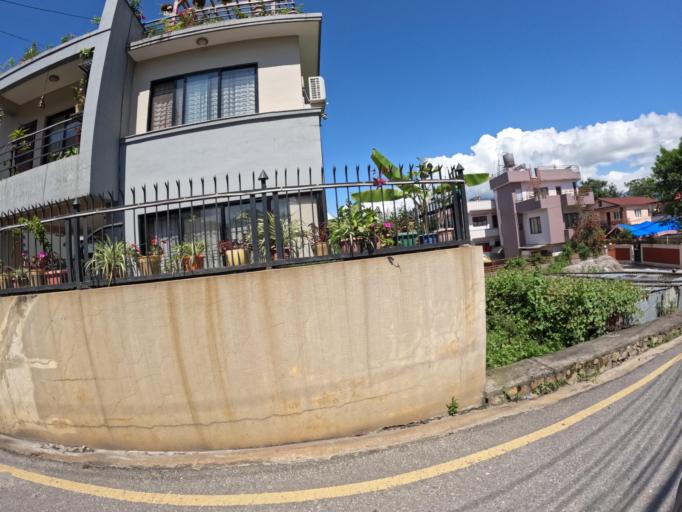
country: NP
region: Central Region
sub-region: Bagmati Zone
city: Kathmandu
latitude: 27.7534
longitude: 85.3314
